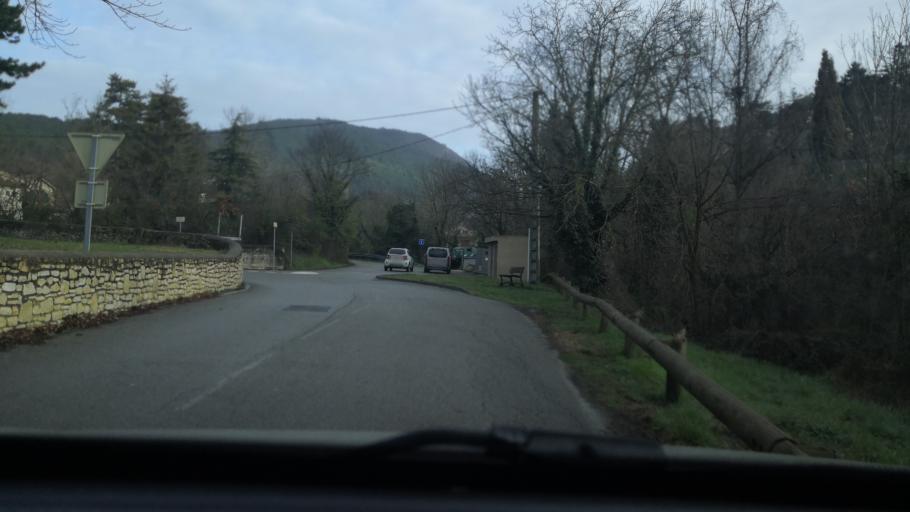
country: FR
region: Rhone-Alpes
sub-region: Departement de la Drome
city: Dieulefit
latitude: 44.5311
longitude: 5.0670
